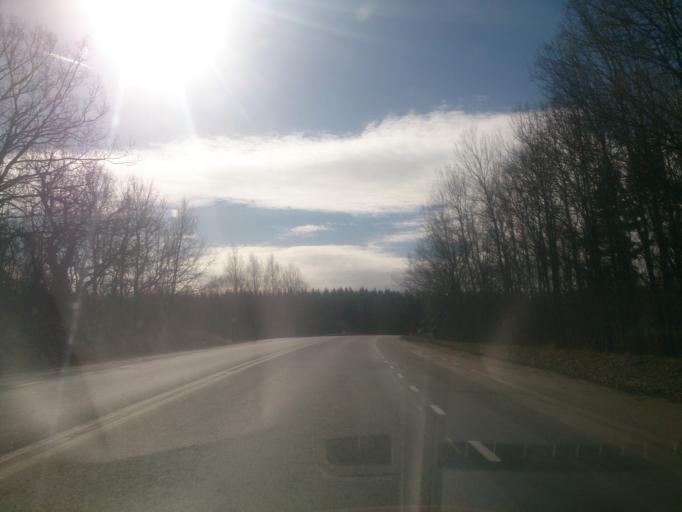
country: SE
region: OEstergoetland
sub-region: Norrkopings Kommun
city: Kimstad
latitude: 58.5068
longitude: 15.9819
